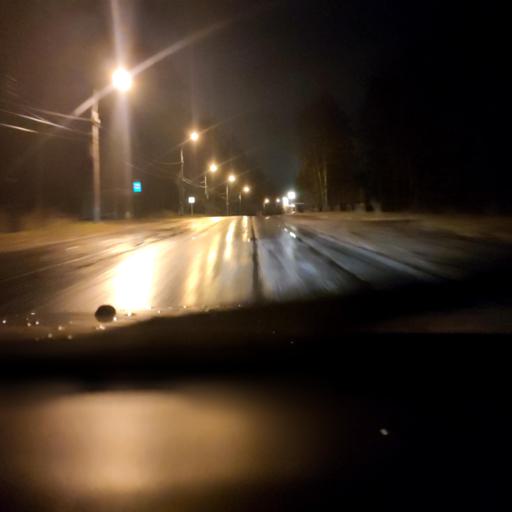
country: RU
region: Perm
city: Kondratovo
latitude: 58.0163
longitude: 55.9964
